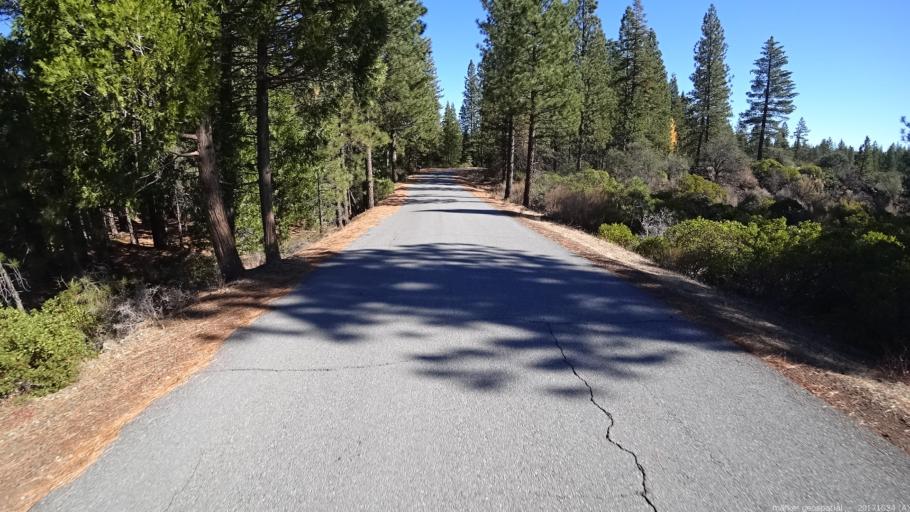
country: US
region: California
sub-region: Shasta County
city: Burney
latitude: 40.7535
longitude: -121.4882
